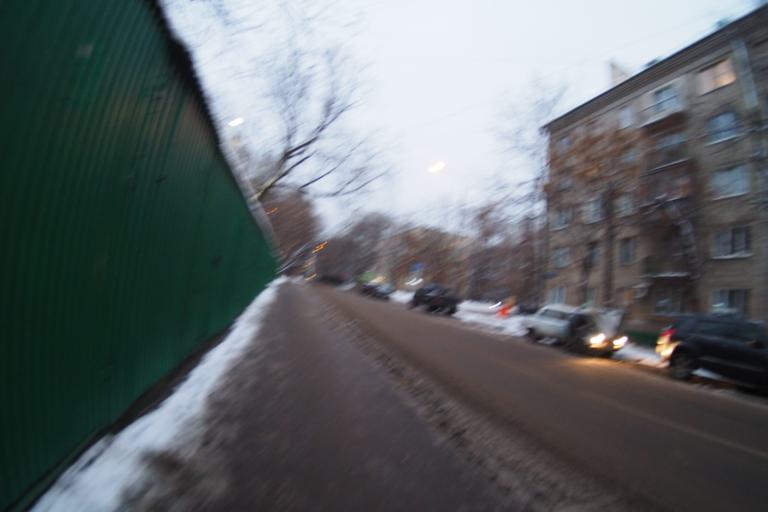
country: RU
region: Moscow
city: Sokol
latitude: 55.8000
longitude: 37.5614
